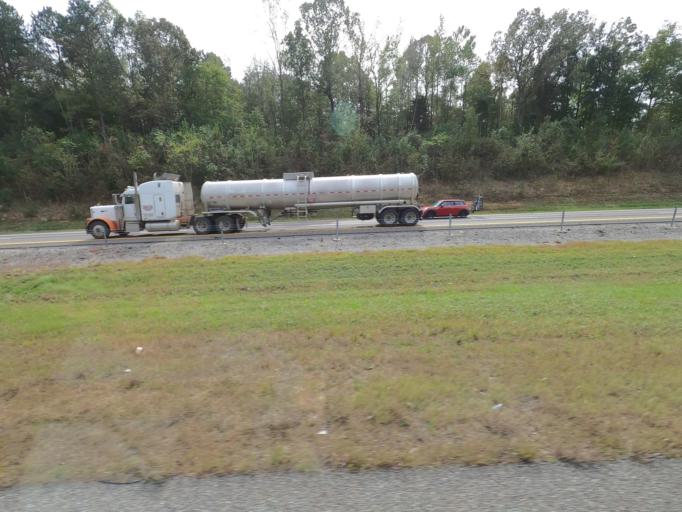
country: US
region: Tennessee
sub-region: Henderson County
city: Lexington
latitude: 35.8147
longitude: -88.2823
